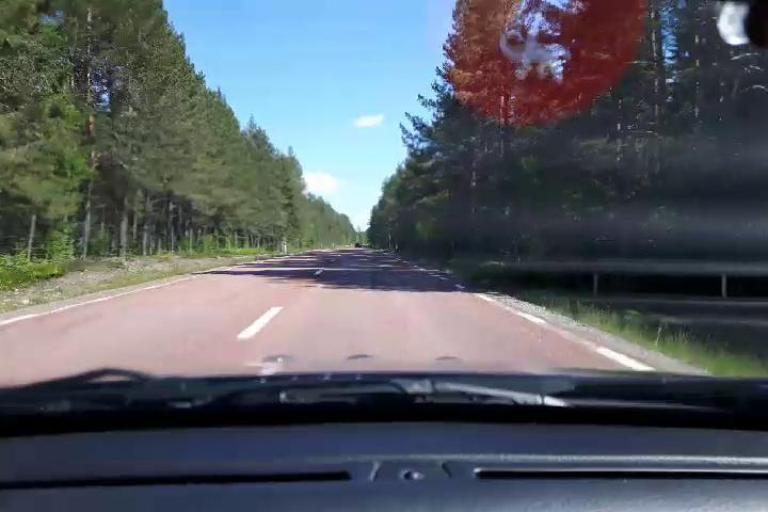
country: SE
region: Gaevleborg
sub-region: Hudiksvalls Kommun
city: Delsbo
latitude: 61.7767
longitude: 16.6611
